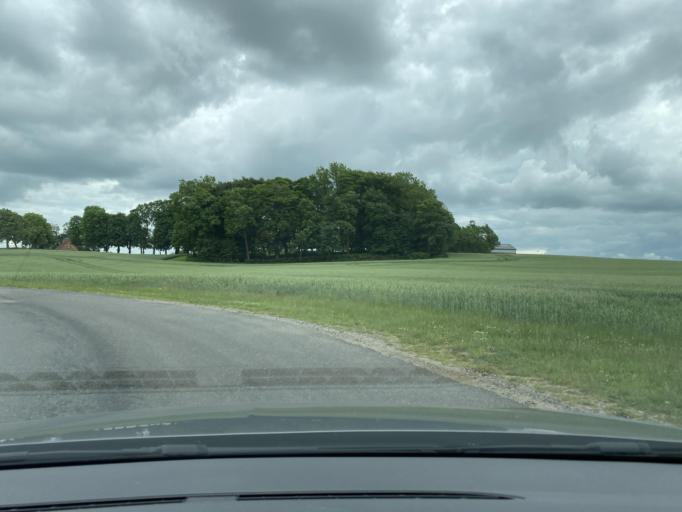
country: DK
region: South Denmark
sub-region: Vejle Kommune
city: Vejle
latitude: 55.6615
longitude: 9.4893
